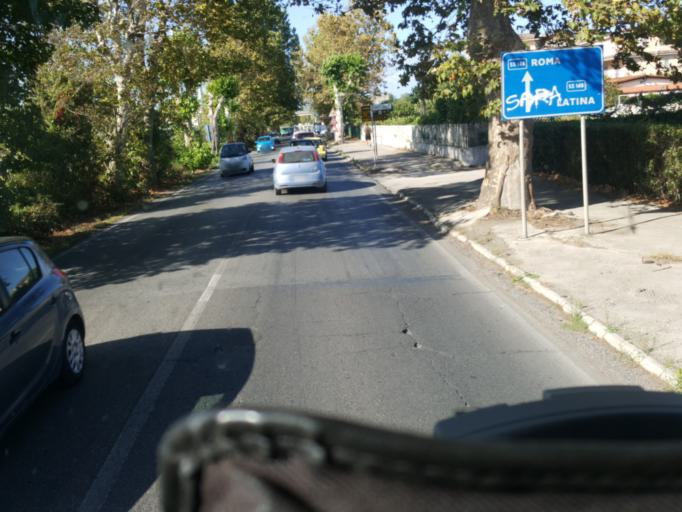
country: IT
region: Latium
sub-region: Provincia di Latina
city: Campo di Carne
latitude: 41.5502
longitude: 12.6353
